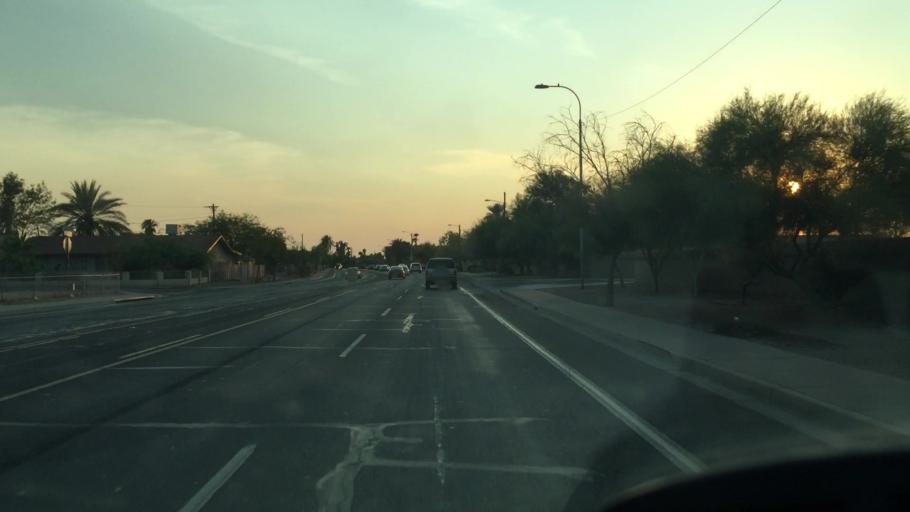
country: US
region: Arizona
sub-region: Maricopa County
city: Phoenix
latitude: 33.3927
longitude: -112.0505
